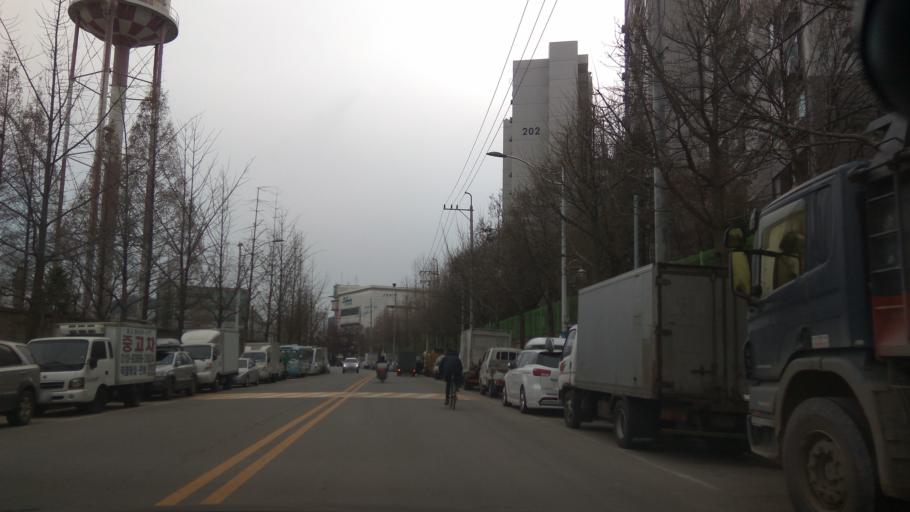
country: KR
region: Incheon
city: Incheon
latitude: 37.4929
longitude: 126.7101
